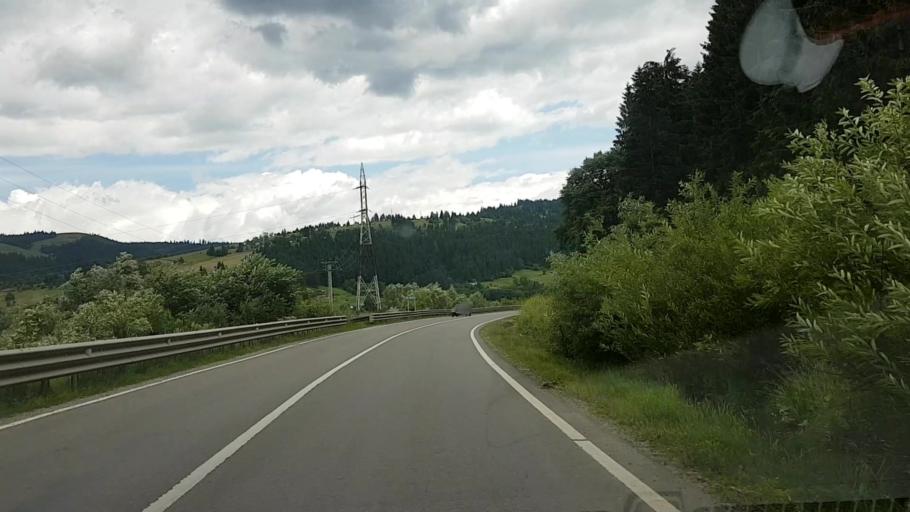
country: RO
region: Neamt
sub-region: Comuna Poiana Teiului
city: Poiana Teiului
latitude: 47.0914
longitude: 25.9571
